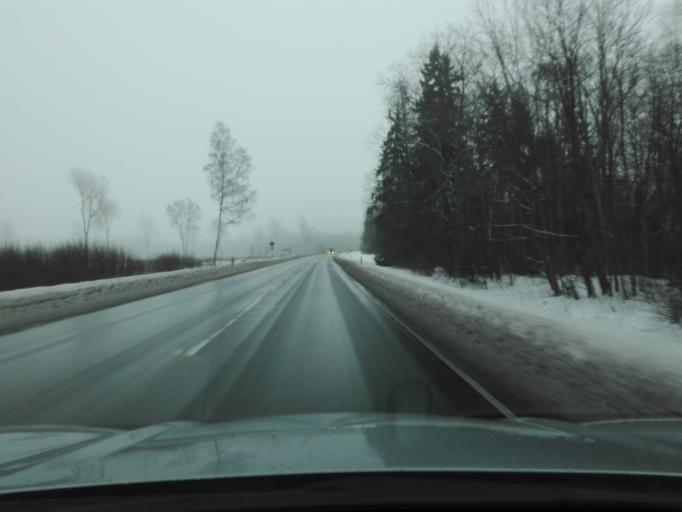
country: EE
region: Raplamaa
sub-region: Kohila vald
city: Kohila
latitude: 59.2336
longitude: 24.7704
